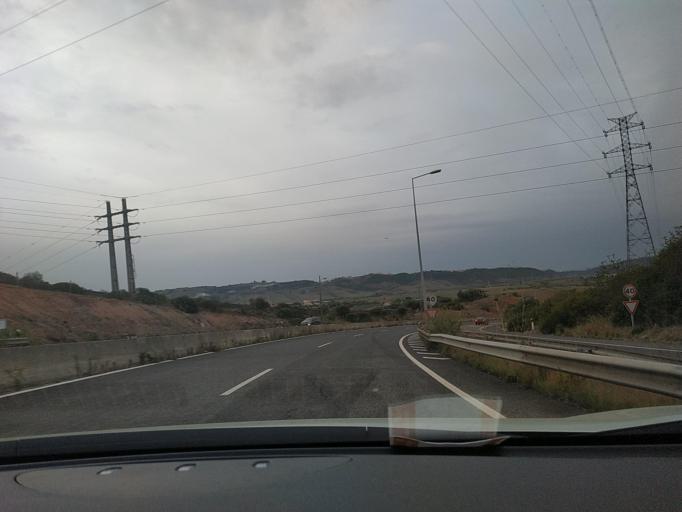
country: PT
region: Lisbon
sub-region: Loures
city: Santo Antao do Tojal
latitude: 38.8631
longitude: -9.1314
